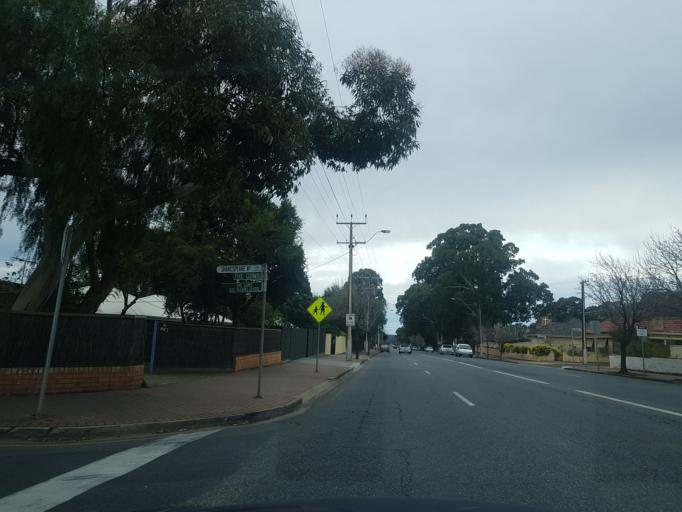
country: AU
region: South Australia
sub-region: Burnside
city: Wattle Park
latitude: -34.9069
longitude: 138.6755
